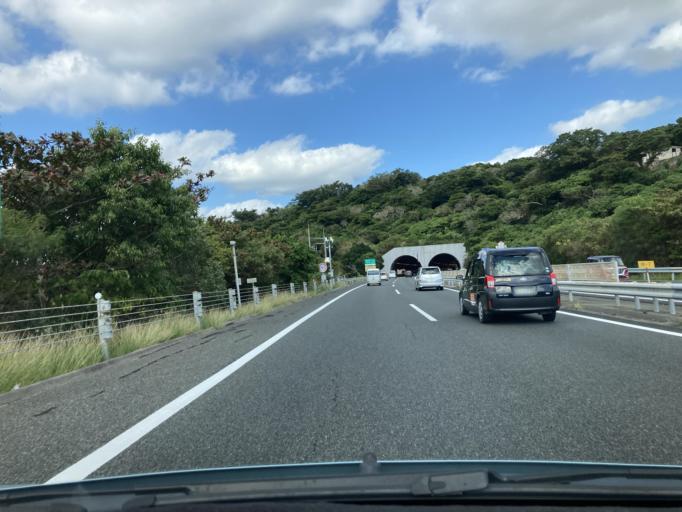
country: JP
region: Okinawa
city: Chatan
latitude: 26.3053
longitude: 127.7898
